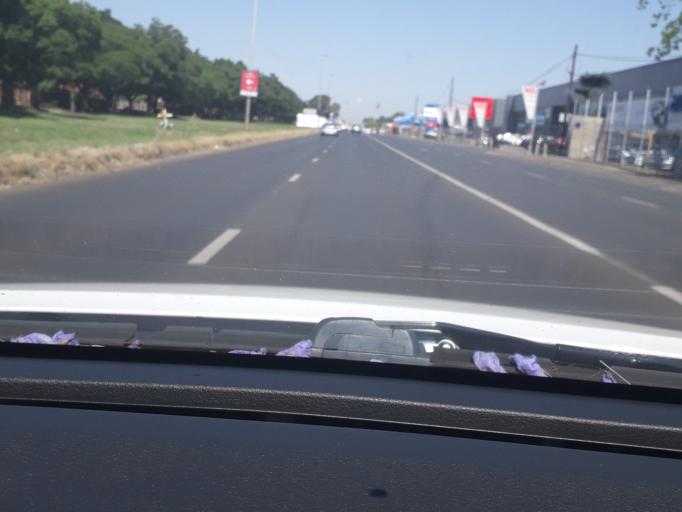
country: ZA
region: Gauteng
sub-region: Ekurhuleni Metropolitan Municipality
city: Boksburg
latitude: -26.1792
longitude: 28.2720
